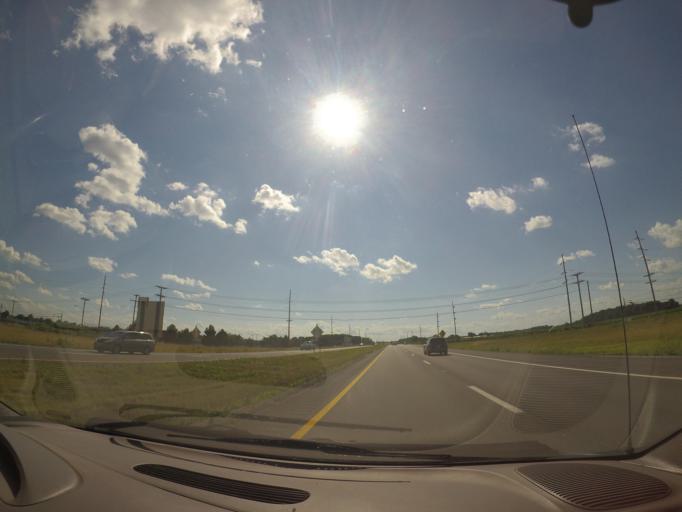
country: US
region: Ohio
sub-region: Sandusky County
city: Fremont
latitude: 41.3683
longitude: -83.1203
